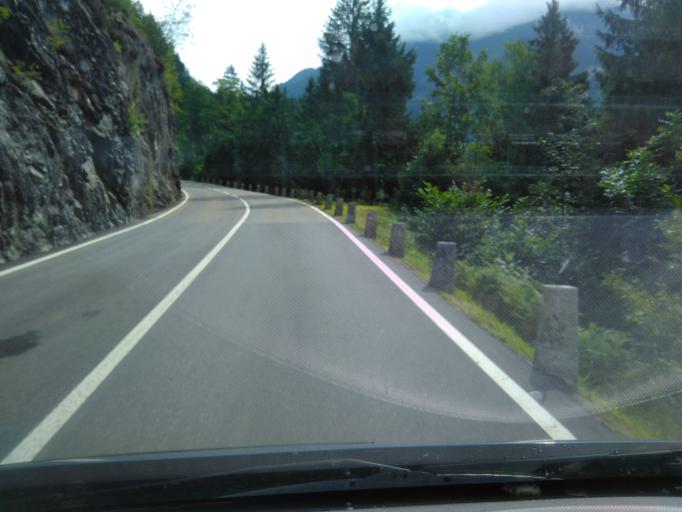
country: CH
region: Bern
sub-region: Interlaken-Oberhasli District
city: Meiringen
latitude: 46.7209
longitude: 8.3085
